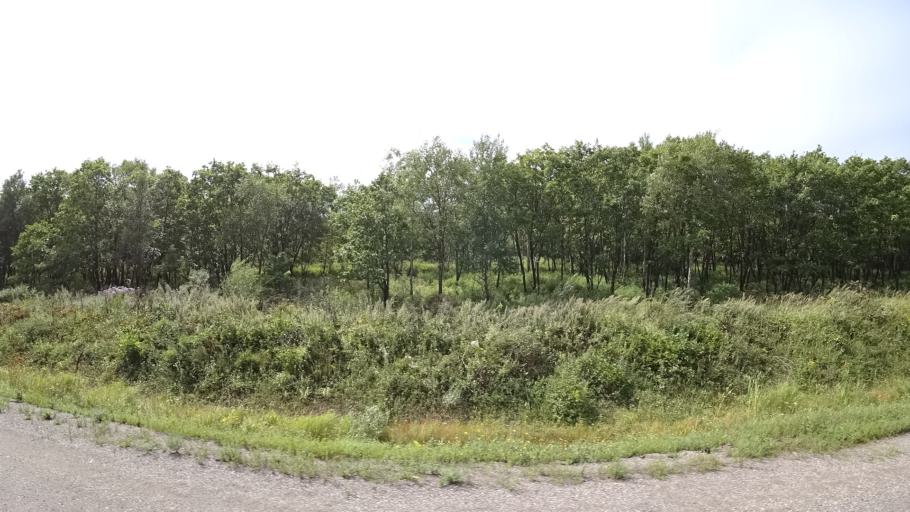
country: RU
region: Primorskiy
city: Lyalichi
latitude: 44.1124
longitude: 132.4198
